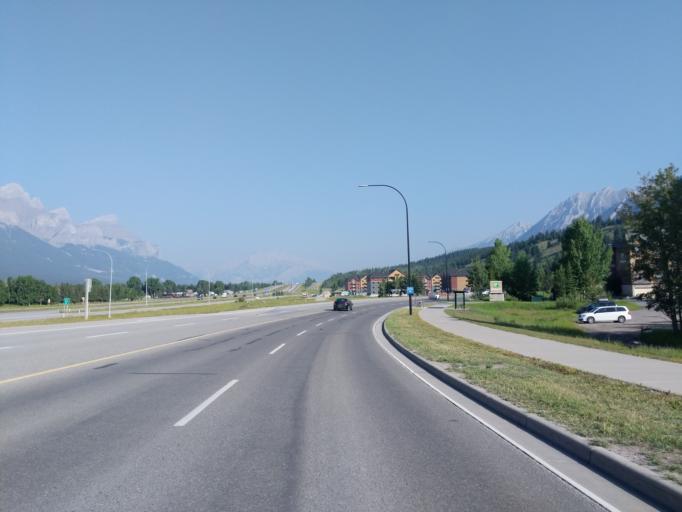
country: CA
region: Alberta
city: Canmore
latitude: 51.0918
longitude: -115.3449
